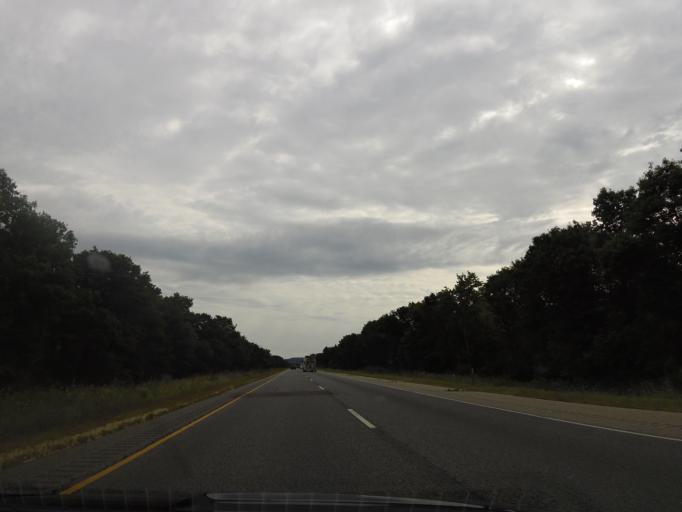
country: US
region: Wisconsin
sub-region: Monroe County
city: Sparta
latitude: 43.9431
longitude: -90.7033
